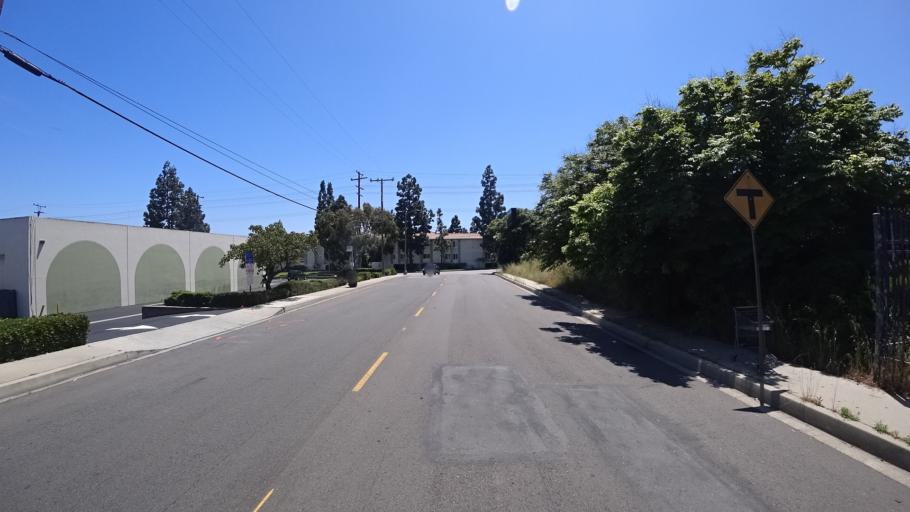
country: US
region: California
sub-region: Los Angeles County
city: Lawndale
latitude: 33.8662
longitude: -118.3566
